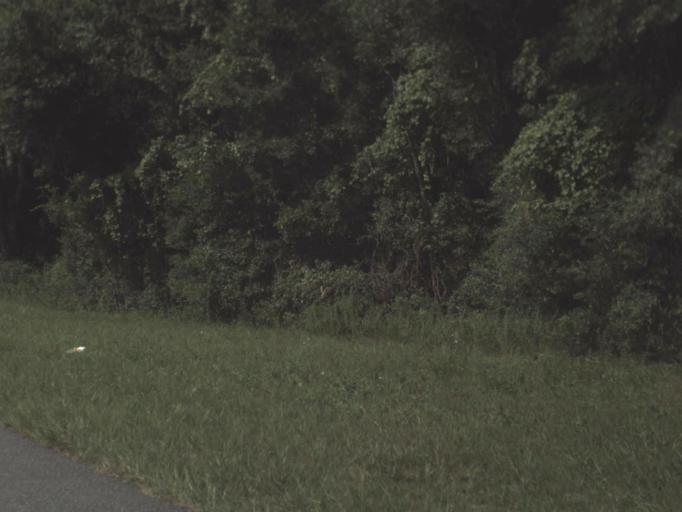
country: US
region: Florida
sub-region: Citrus County
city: Hernando
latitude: 28.9268
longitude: -82.3915
